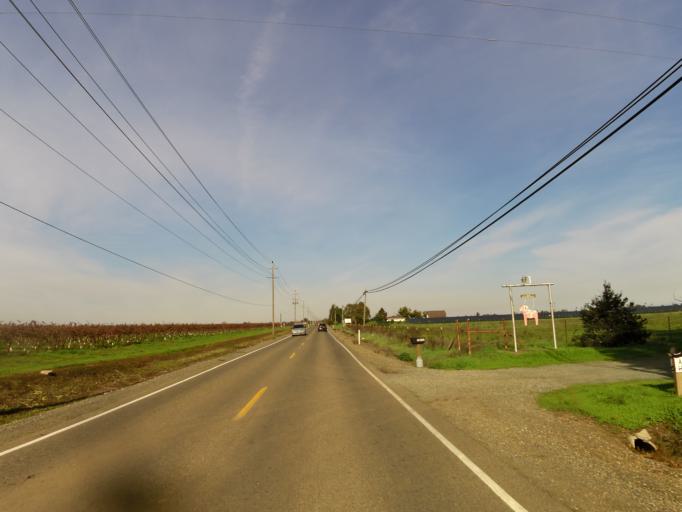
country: US
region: California
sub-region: Sacramento County
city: Laguna
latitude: 38.3599
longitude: -121.4175
